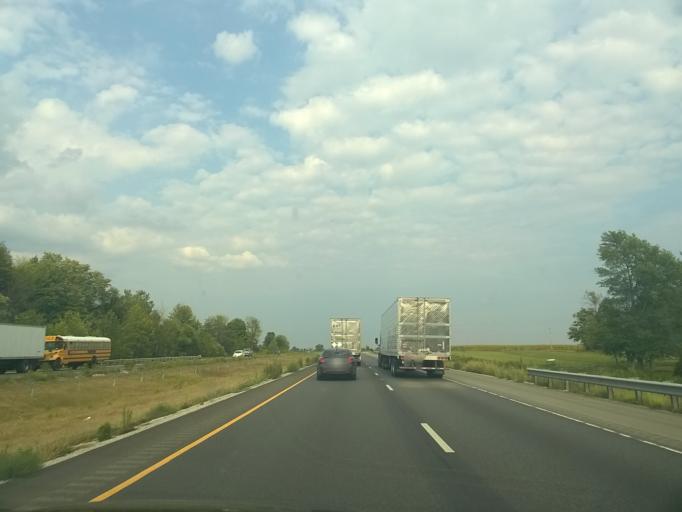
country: US
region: Indiana
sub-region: Clay County
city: Brazil
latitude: 39.4690
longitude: -87.0360
